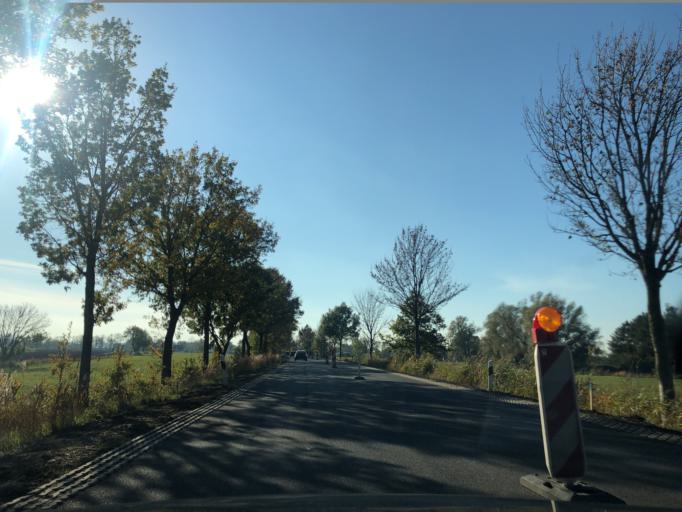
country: DE
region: Lower Saxony
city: Lemwerder
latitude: 53.1541
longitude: 8.5536
